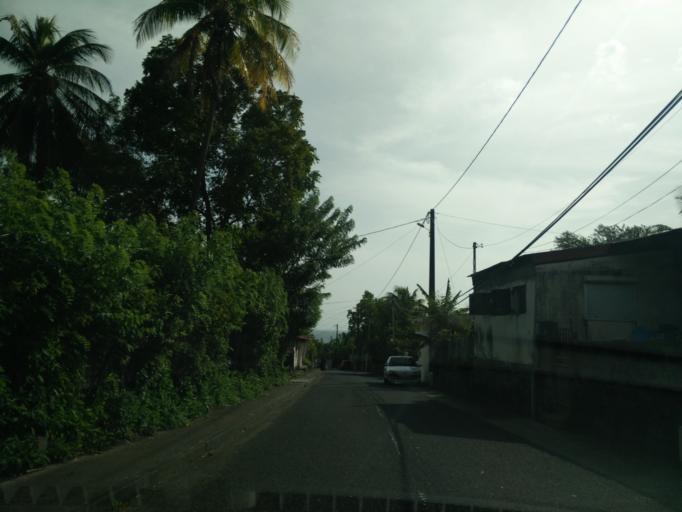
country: MQ
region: Martinique
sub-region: Martinique
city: Saint-Pierre
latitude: 14.7524
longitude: -61.1762
